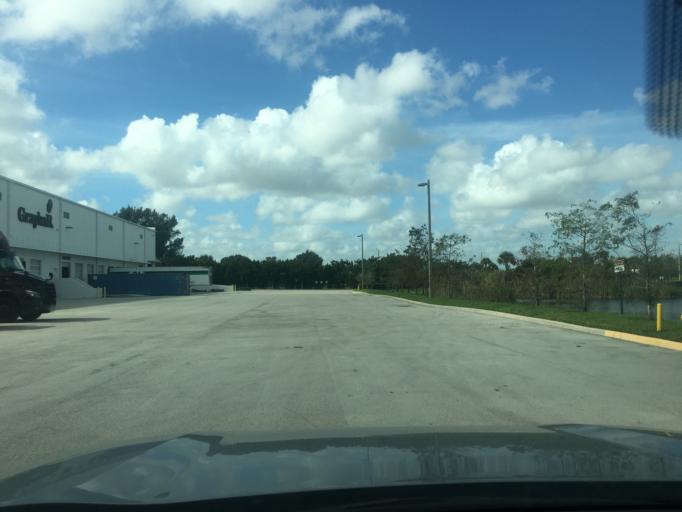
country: US
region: Florida
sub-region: Broward County
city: Broadview Park
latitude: 26.0808
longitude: -80.1795
